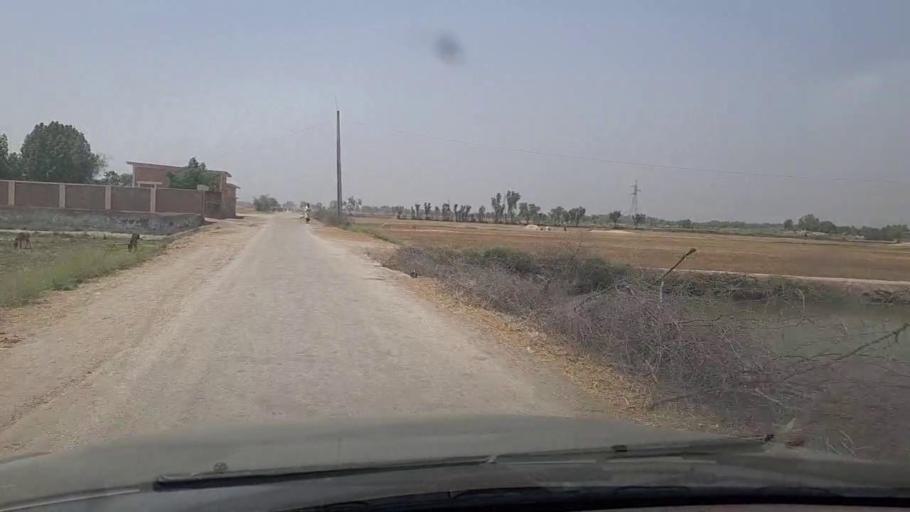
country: PK
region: Sindh
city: Ratodero
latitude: 27.7971
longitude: 68.2576
